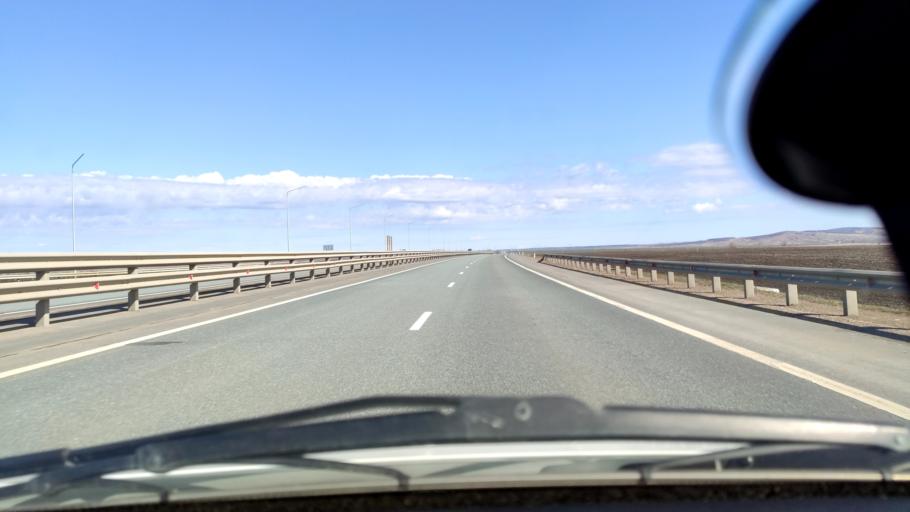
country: RU
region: Bashkortostan
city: Tolbazy
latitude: 54.2086
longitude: 55.8832
